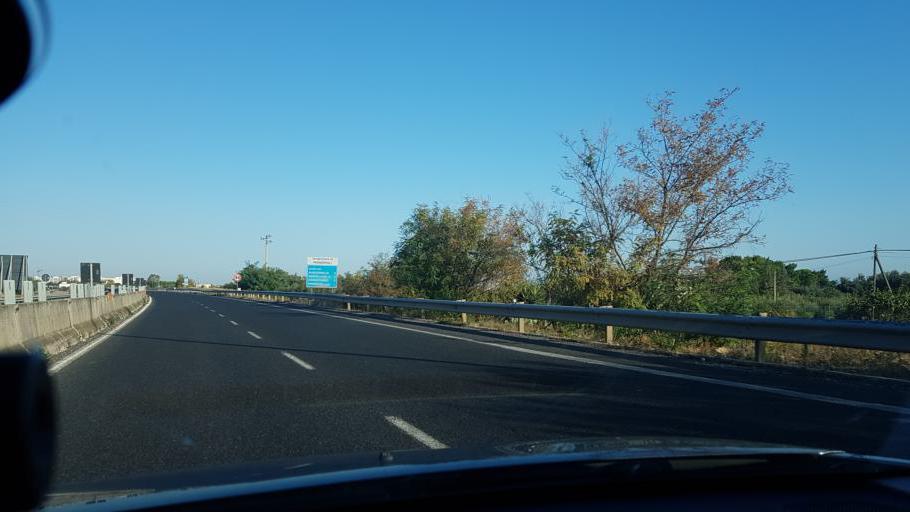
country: IT
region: Apulia
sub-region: Provincia di Bari
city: Monopoli
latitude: 40.9235
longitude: 17.3143
